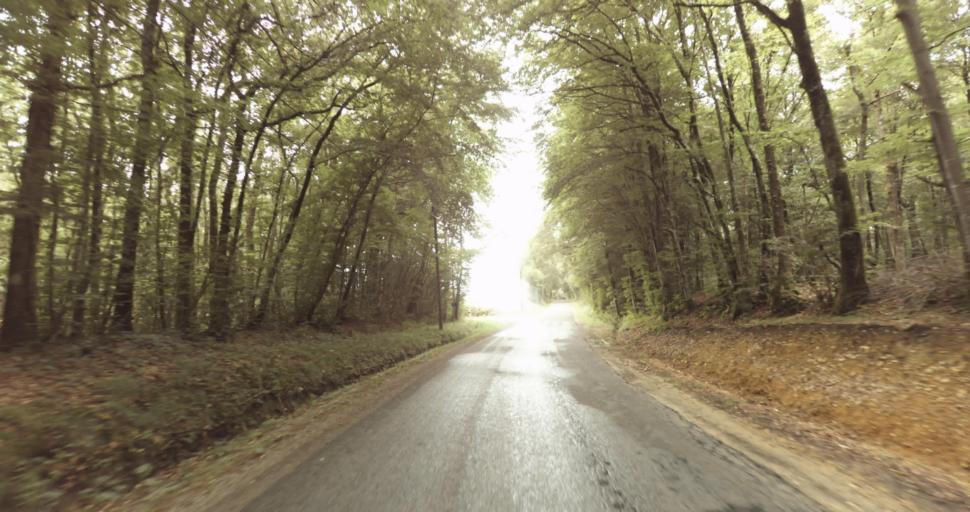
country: FR
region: Lower Normandy
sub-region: Departement de l'Orne
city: Sainte-Gauburge-Sainte-Colombe
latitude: 48.7569
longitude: 0.3883
